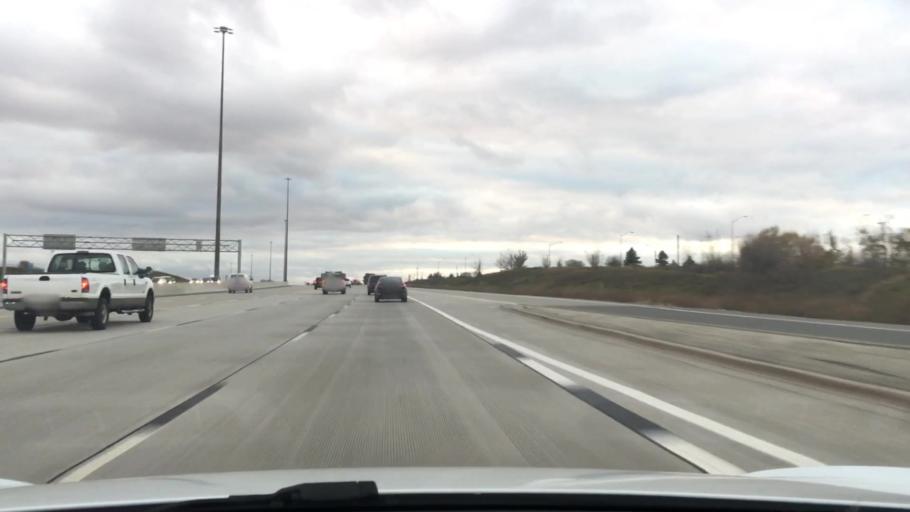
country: CA
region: Ontario
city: Concord
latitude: 43.8268
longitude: -79.4585
